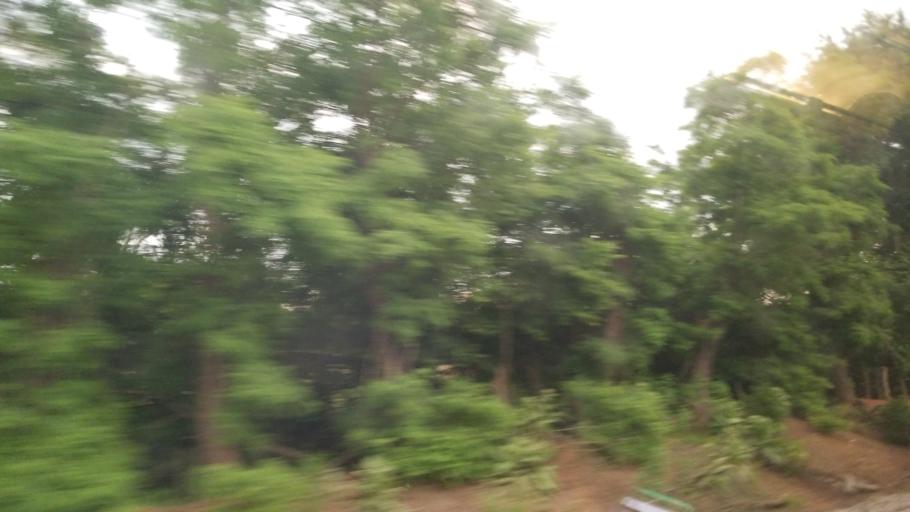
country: US
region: Virginia
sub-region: Culpeper County
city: Culpeper
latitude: 38.4284
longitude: -77.9990
